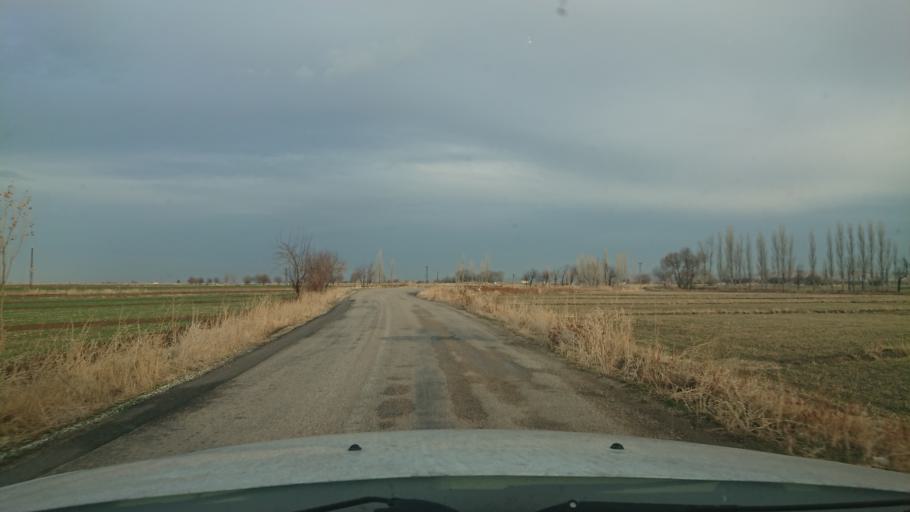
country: TR
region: Aksaray
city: Yesilova
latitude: 38.4411
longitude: 33.8370
